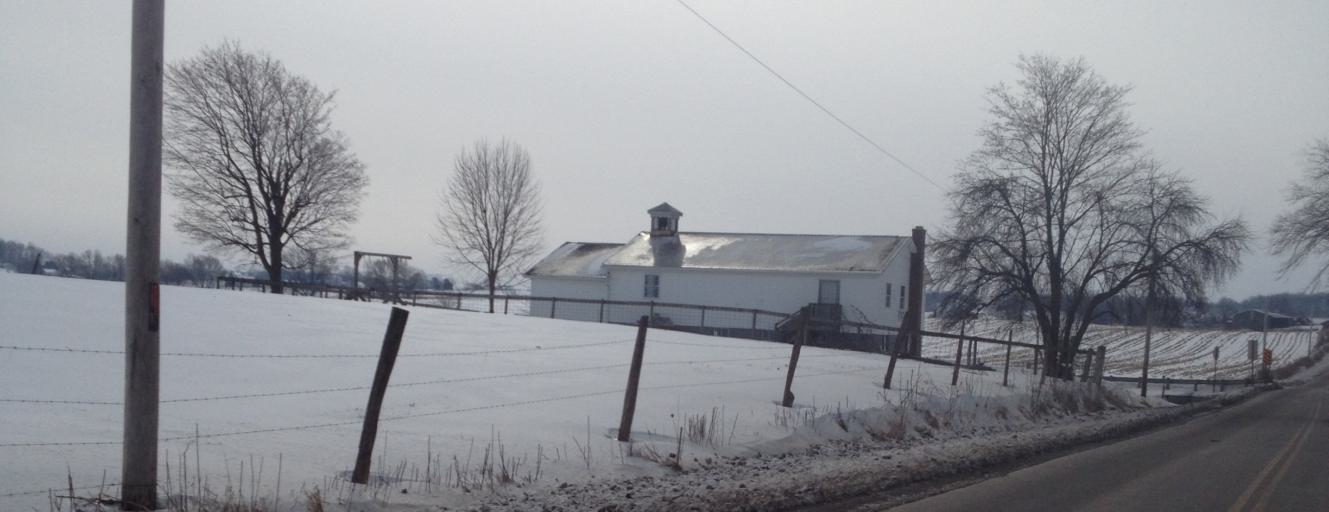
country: US
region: Ohio
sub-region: Wayne County
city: Apple Creek
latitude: 40.6836
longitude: -81.7840
